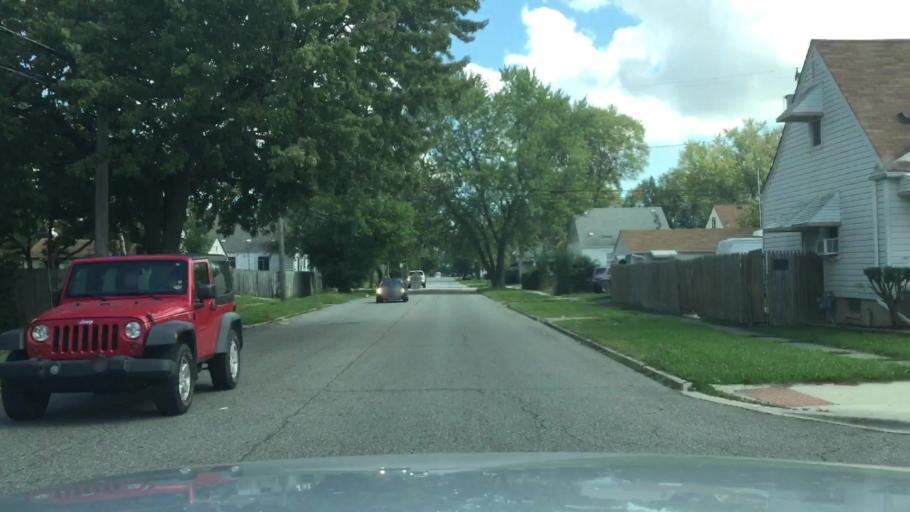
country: US
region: Michigan
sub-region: Wayne County
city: Dearborn
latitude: 42.3360
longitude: -83.2205
